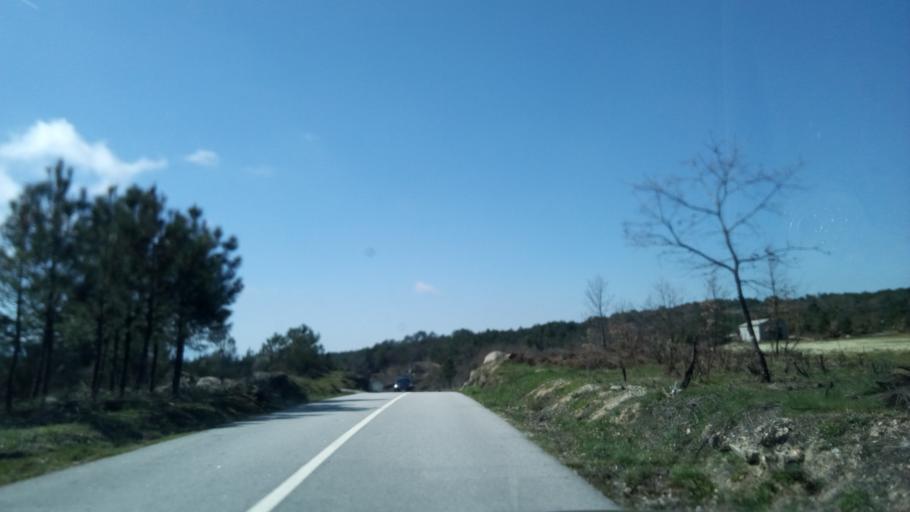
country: PT
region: Guarda
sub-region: Fornos de Algodres
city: Fornos de Algodres
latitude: 40.6391
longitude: -7.5322
